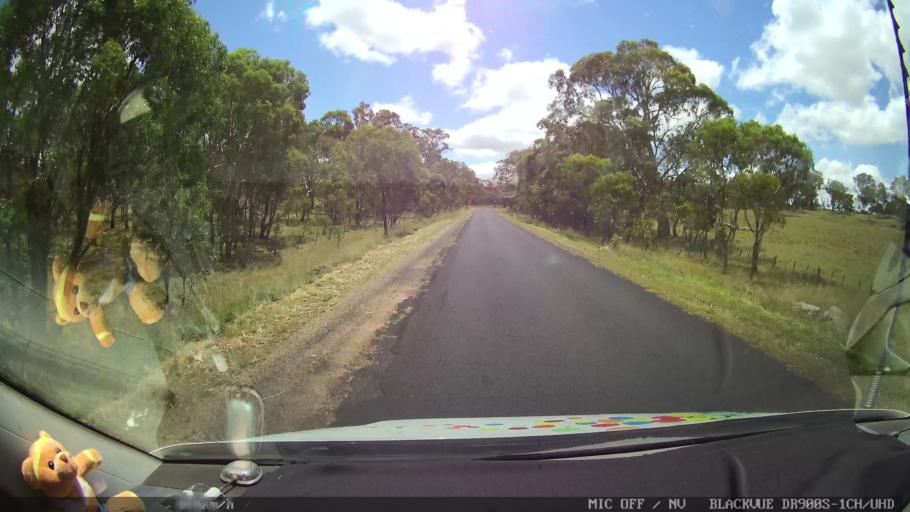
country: AU
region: New South Wales
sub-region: Glen Innes Severn
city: Glen Innes
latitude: -29.4330
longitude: 151.6846
